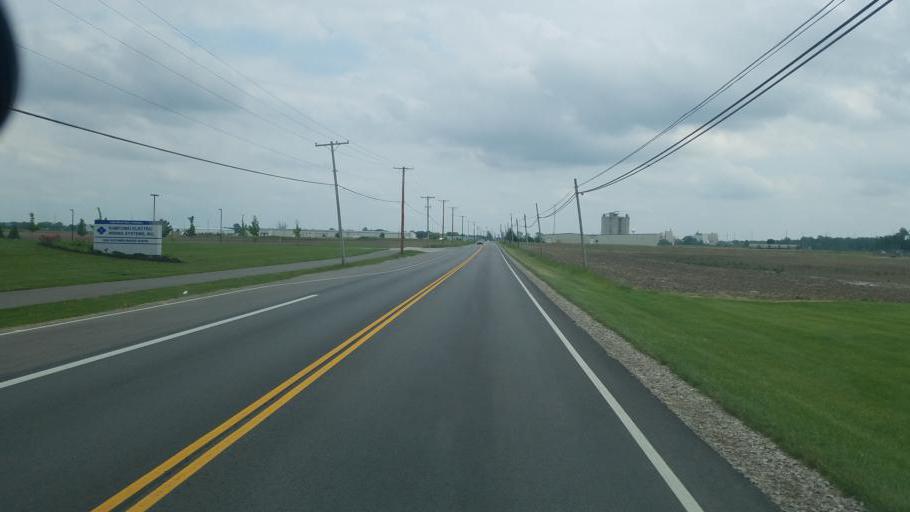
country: US
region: Ohio
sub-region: Union County
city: Marysville
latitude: 40.2199
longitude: -83.3330
